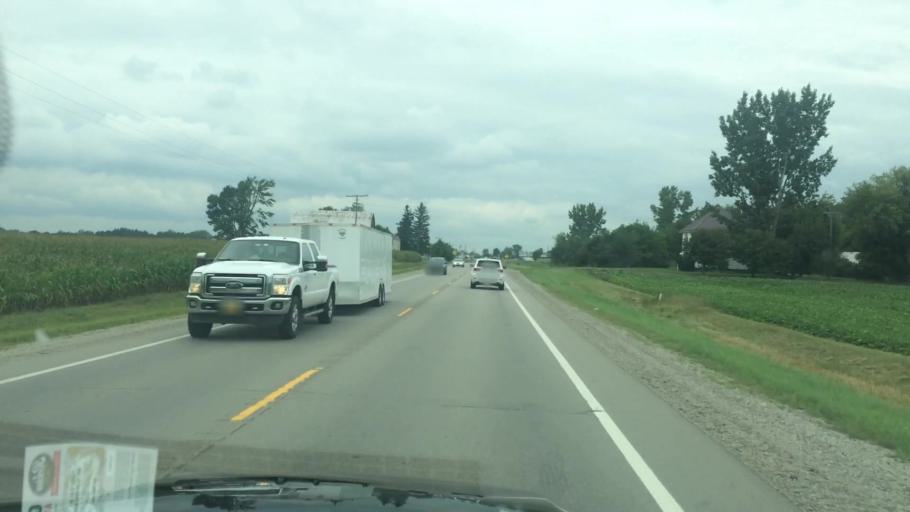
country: US
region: Michigan
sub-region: Sanilac County
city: Marlette
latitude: 43.4080
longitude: -83.0869
